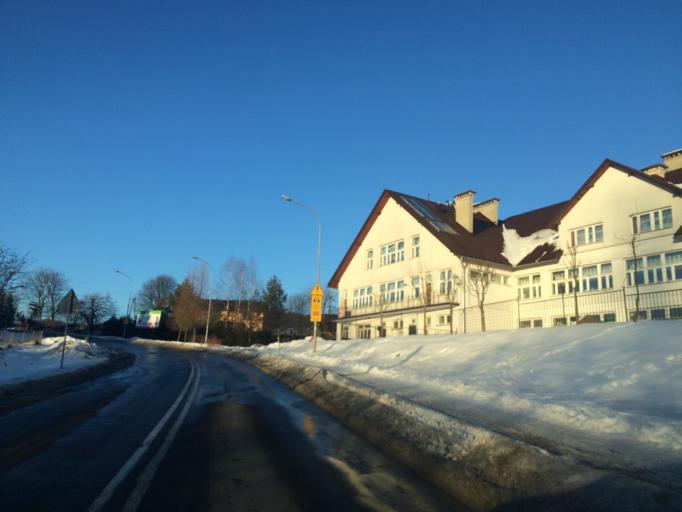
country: PL
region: Subcarpathian Voivodeship
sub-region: Powiat bieszczadzki
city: Lutowiska
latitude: 49.2498
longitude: 22.6959
